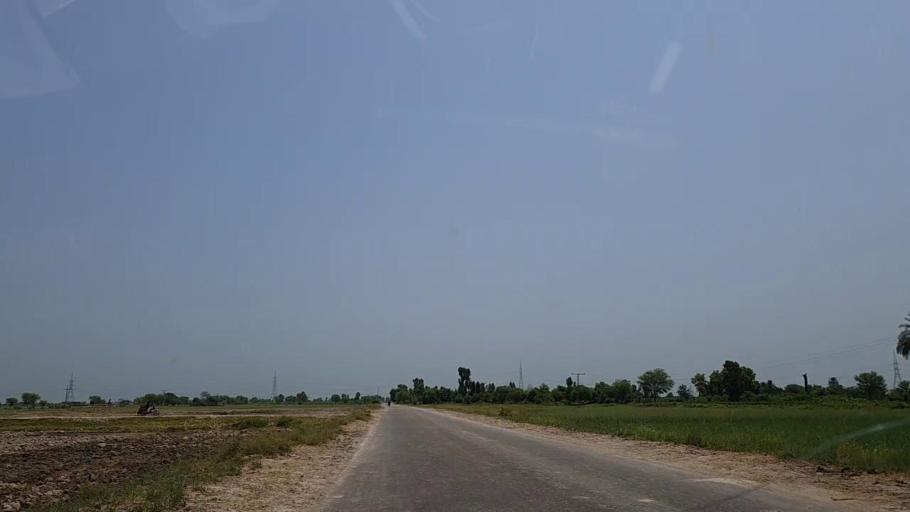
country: PK
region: Sindh
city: Ghotki
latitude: 27.9864
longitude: 69.3662
